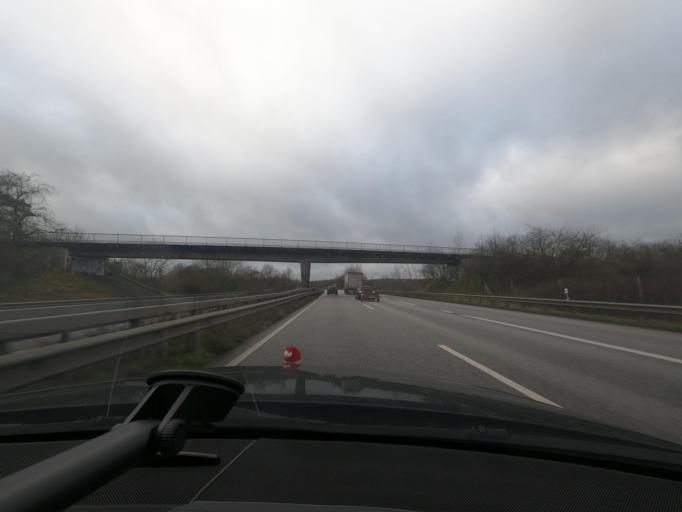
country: DE
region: Schleswig-Holstein
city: Datgen
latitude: 54.1891
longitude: 9.9293
